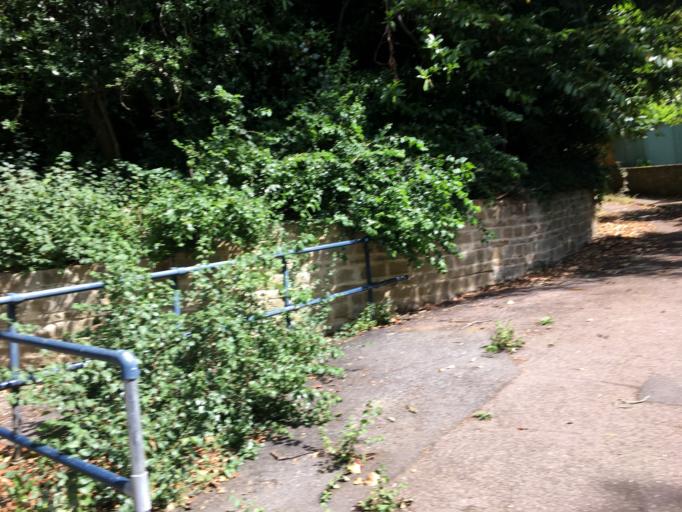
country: GB
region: England
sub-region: Surrey
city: Reigate
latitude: 51.2291
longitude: -0.2026
